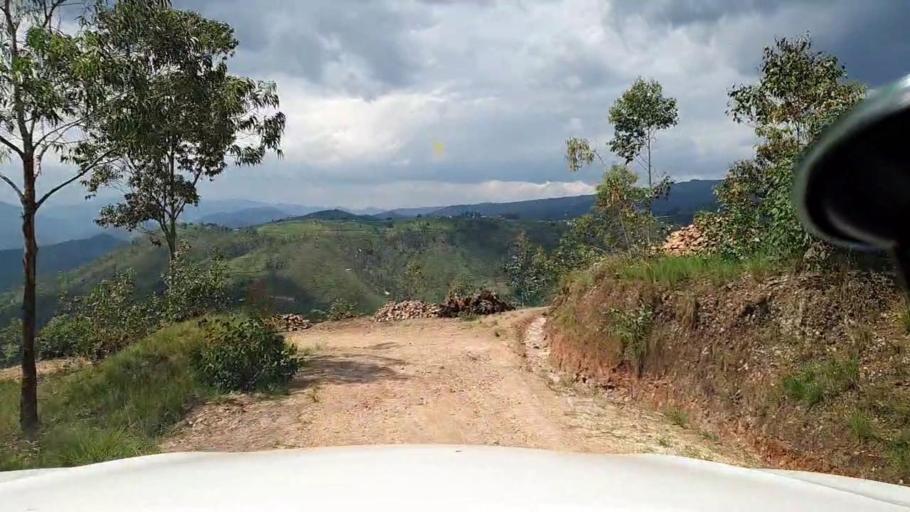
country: RW
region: Southern Province
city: Gitarama
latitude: -1.8407
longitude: 29.8211
